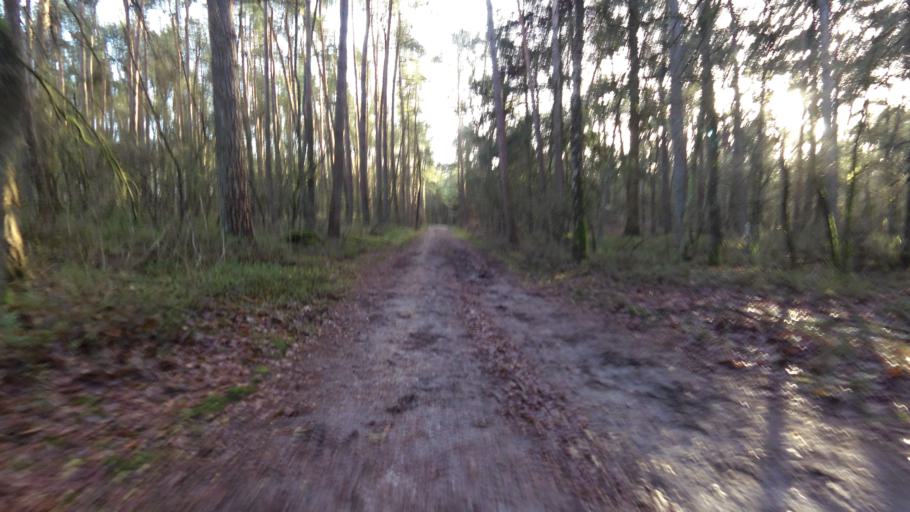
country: NL
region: Gelderland
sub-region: Gemeente Epe
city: Vaassen
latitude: 52.2627
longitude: 5.9190
